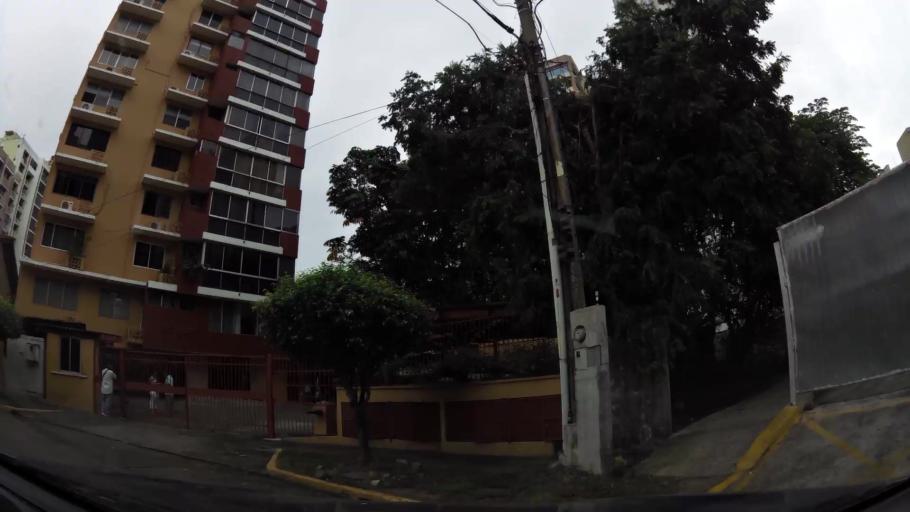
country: PA
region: Panama
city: Panama
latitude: 8.9776
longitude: -79.5194
